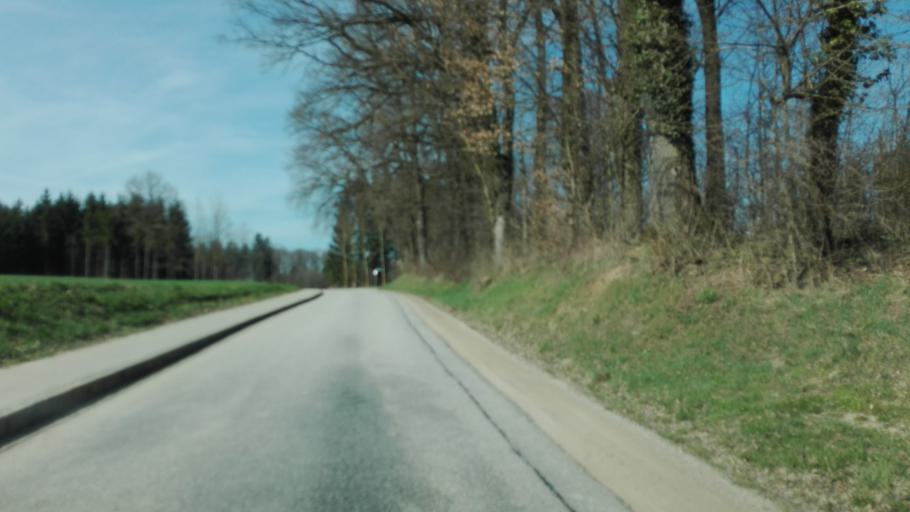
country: AT
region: Lower Austria
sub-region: Politischer Bezirk Amstetten
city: Ennsdorf
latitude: 48.2501
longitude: 14.5205
